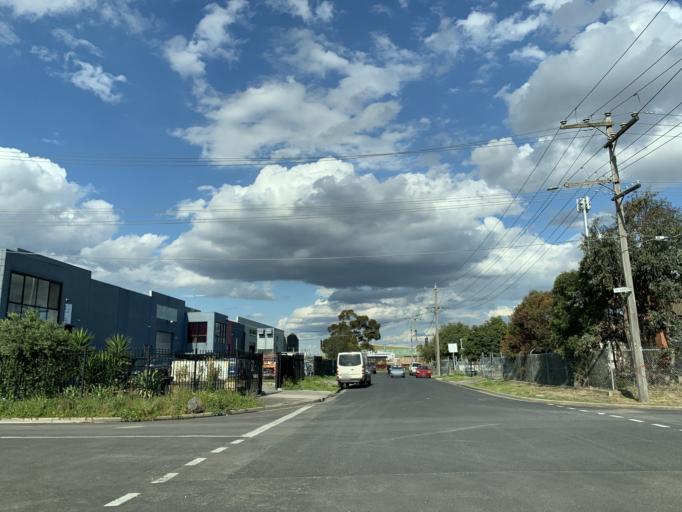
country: AU
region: Victoria
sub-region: Brimbank
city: Albion
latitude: -37.7606
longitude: 144.8365
